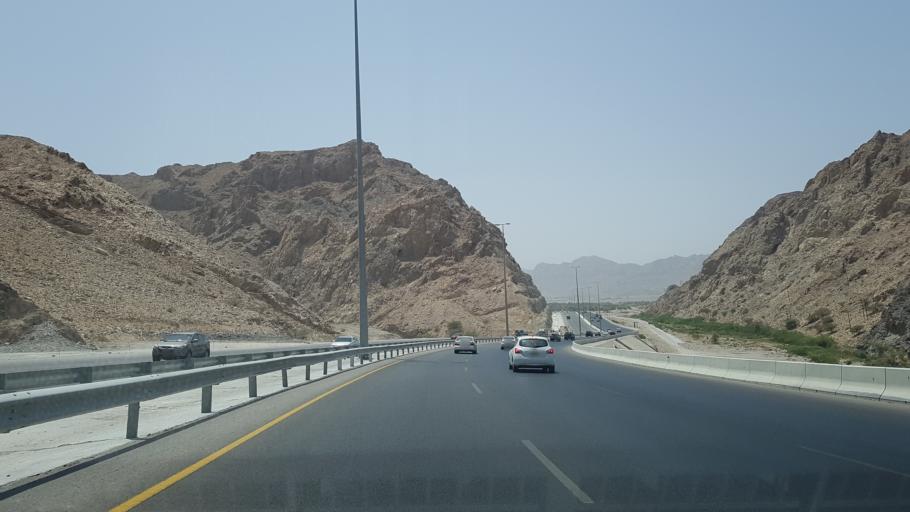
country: OM
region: Muhafazat Masqat
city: Muscat
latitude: 23.5392
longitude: 58.5263
